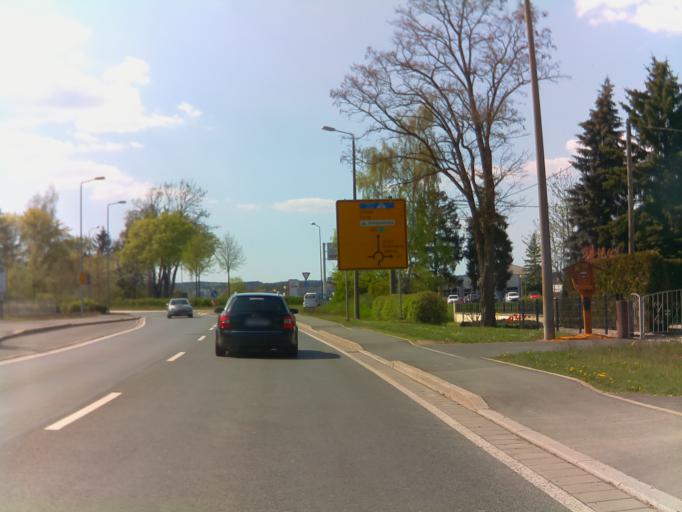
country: DE
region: Saxony
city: Syrau
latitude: 50.5354
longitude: 12.1022
